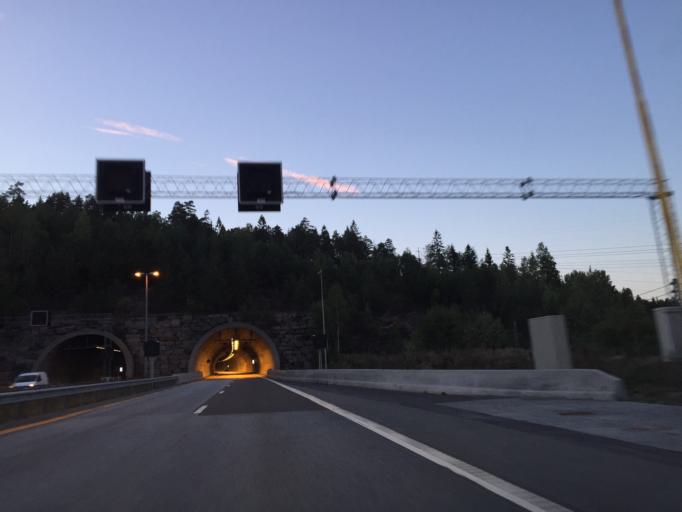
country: NO
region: Akershus
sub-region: Vestby
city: Vestby
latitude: 59.5264
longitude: 10.7299
